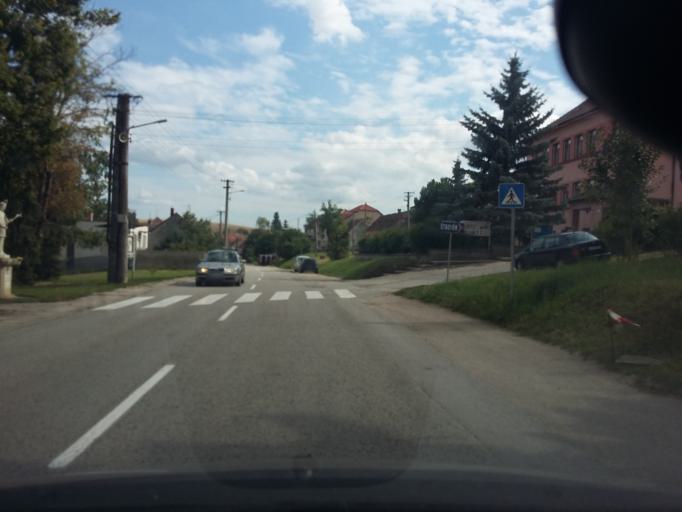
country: SK
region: Trnavsky
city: Gbely
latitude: 48.7209
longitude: 17.1607
